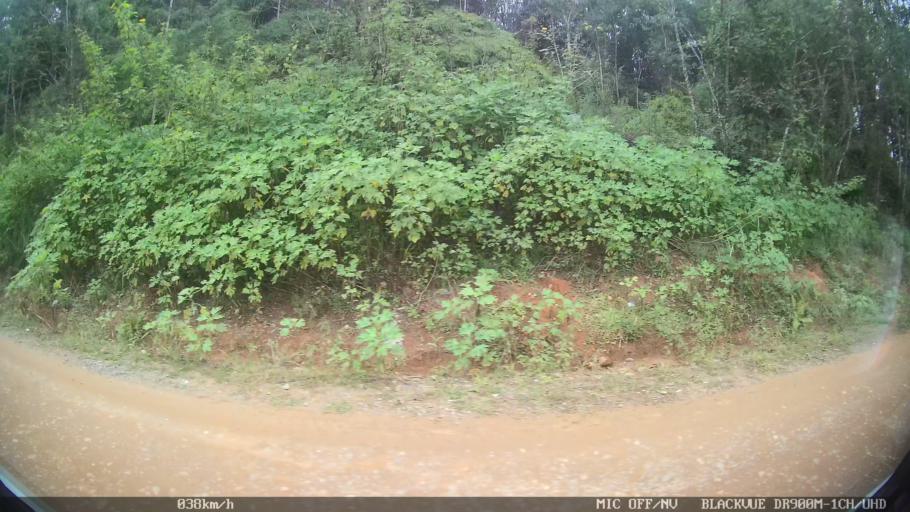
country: BR
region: Santa Catarina
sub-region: Joinville
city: Joinville
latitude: -26.2726
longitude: -48.9029
